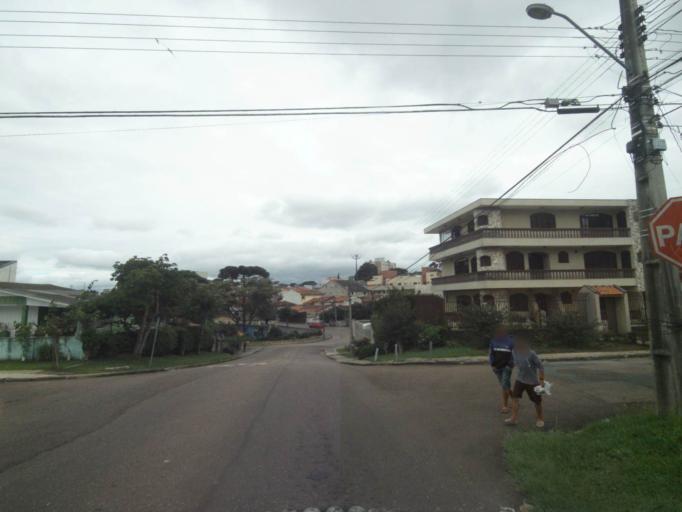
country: BR
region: Parana
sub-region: Curitiba
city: Curitiba
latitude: -25.4860
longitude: -49.2891
